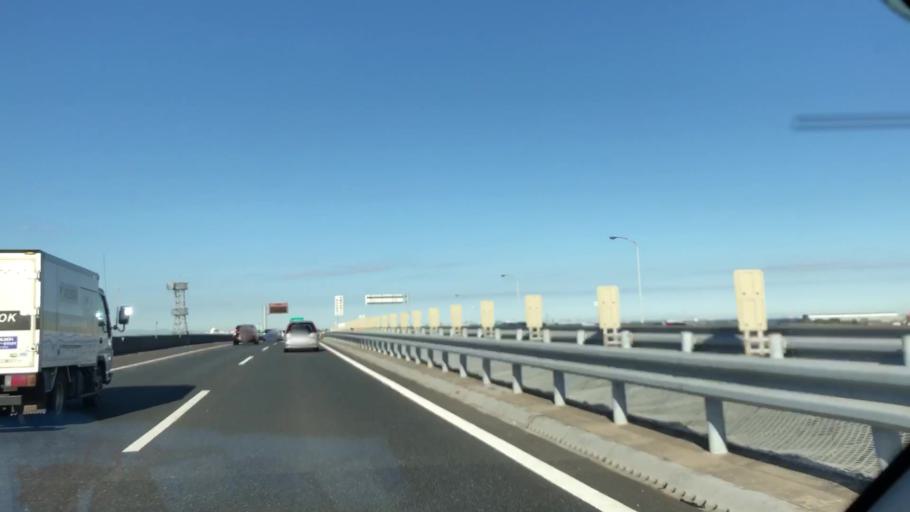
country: JP
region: Chiba
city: Kisarazu
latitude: 35.4245
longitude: 139.9325
